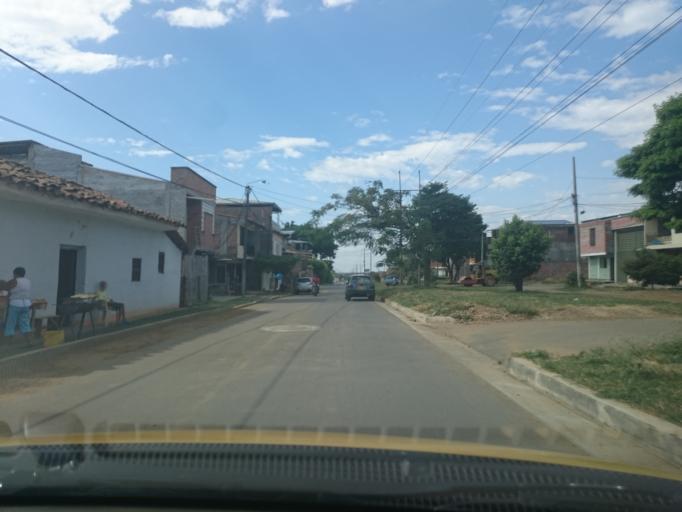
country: CO
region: Cauca
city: Santander de Quilichao
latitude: 3.0144
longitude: -76.4881
